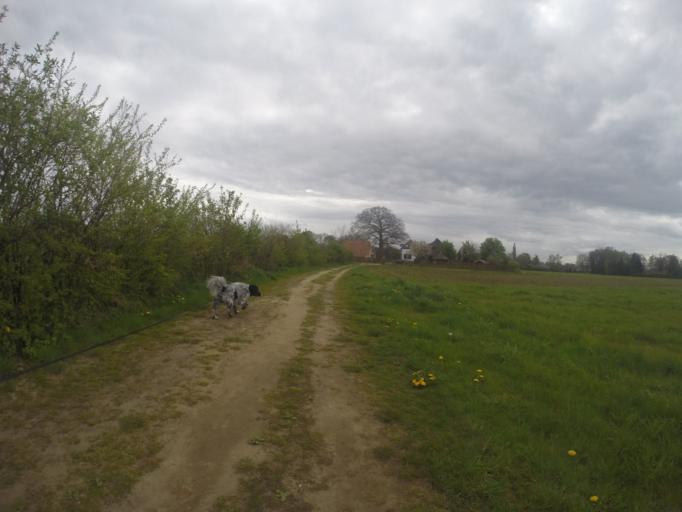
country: NL
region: Gelderland
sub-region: Gemeente Bronckhorst
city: Baak
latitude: 52.0930
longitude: 6.2623
